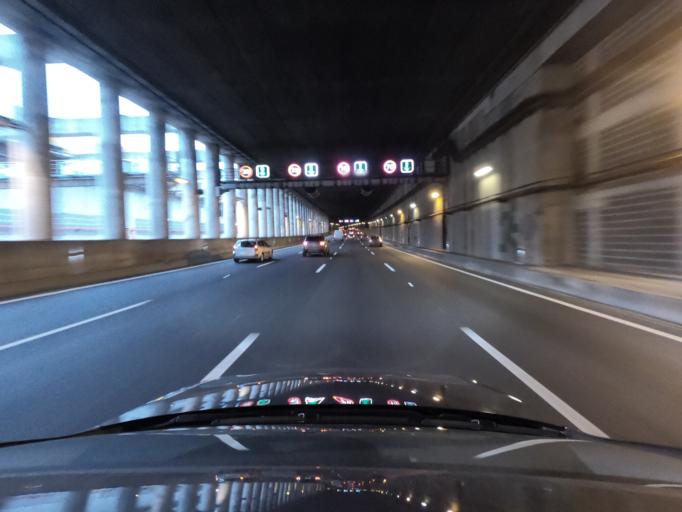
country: PT
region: Lisbon
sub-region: Amadora
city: Amadora
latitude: 38.7490
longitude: -9.2106
